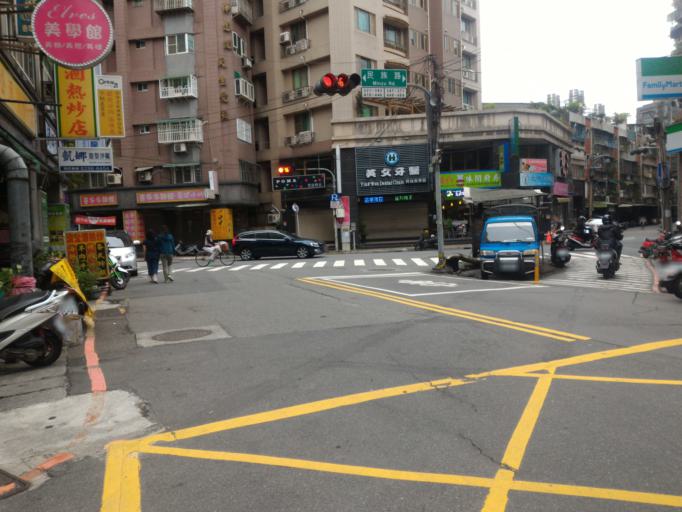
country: TW
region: Taipei
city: Taipei
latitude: 25.0922
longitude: 121.4727
